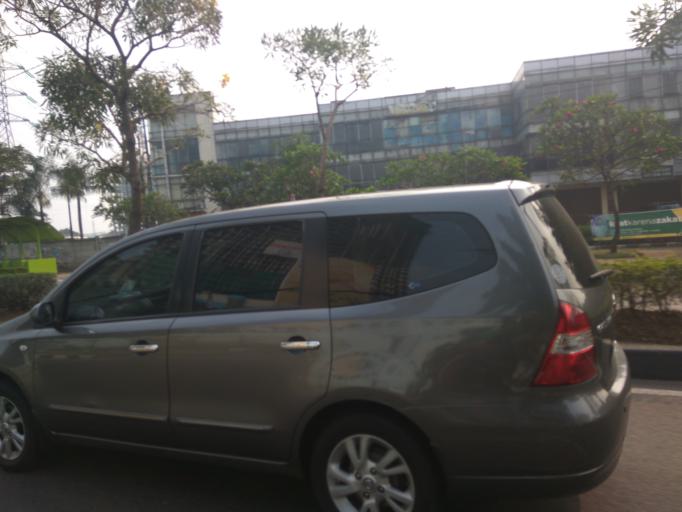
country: ID
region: West Java
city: Bekasi
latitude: -6.2610
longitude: 106.9973
